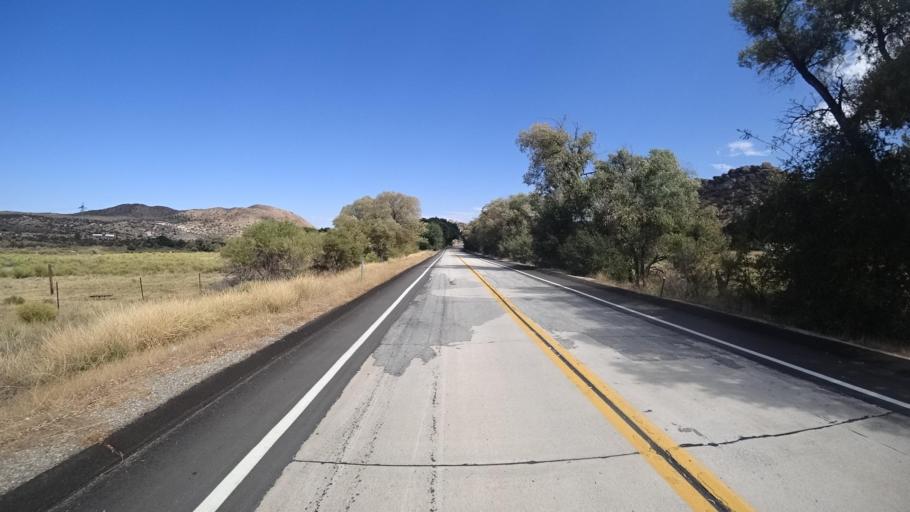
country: MX
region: Baja California
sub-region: Tecate
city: Cereso del Hongo
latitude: 32.6610
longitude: -116.2546
